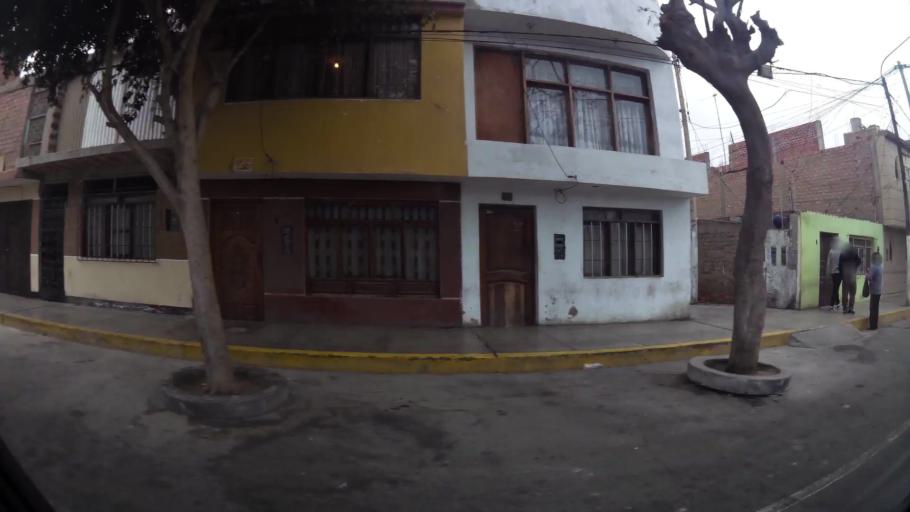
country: PE
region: Ancash
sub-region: Provincia de Santa
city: Chimbote
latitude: -9.0710
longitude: -78.5866
